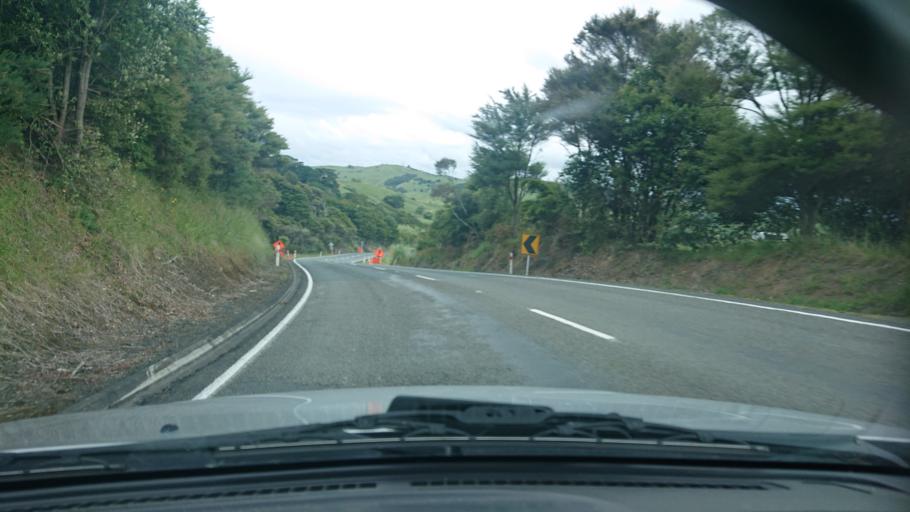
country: NZ
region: Auckland
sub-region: Auckland
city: Wellsford
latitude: -36.3691
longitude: 174.4526
